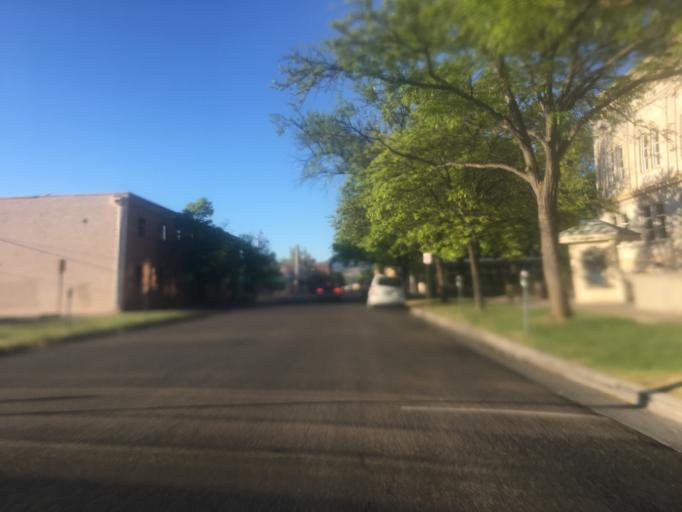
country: US
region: Colorado
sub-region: Mesa County
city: Grand Junction
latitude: 39.0691
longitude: -108.5627
